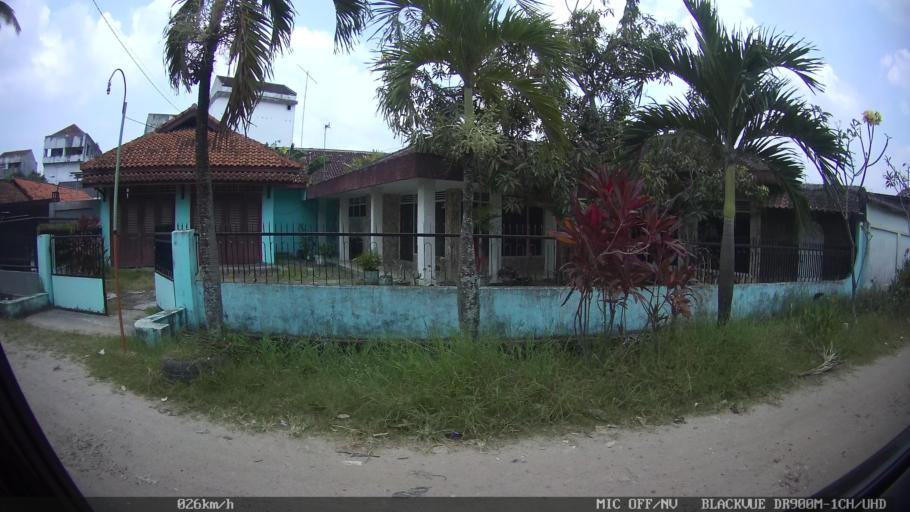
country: ID
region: Lampung
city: Pringsewu
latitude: -5.3527
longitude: 104.9776
